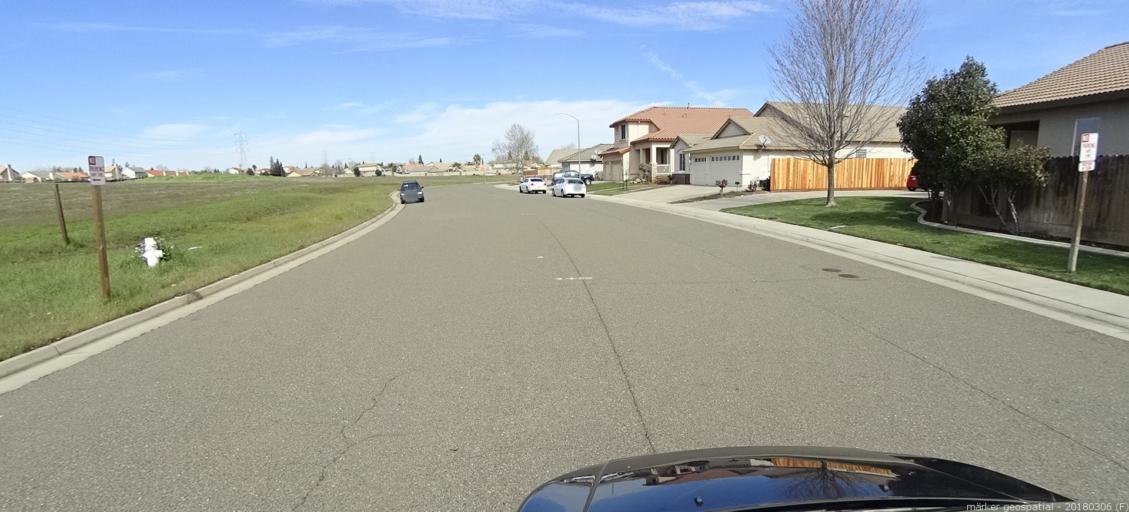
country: US
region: California
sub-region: Sacramento County
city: Vineyard
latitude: 38.4607
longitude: -121.3408
